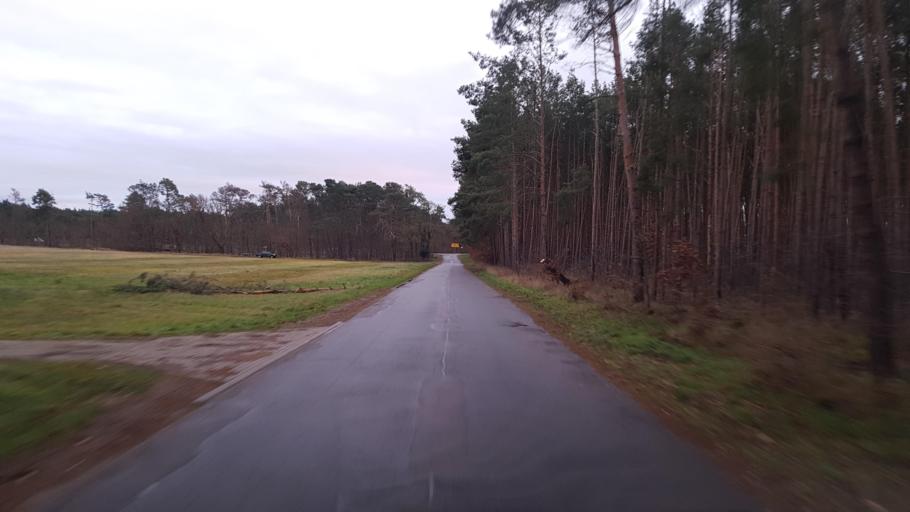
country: DE
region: Brandenburg
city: Luebben
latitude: 51.9015
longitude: 13.8136
